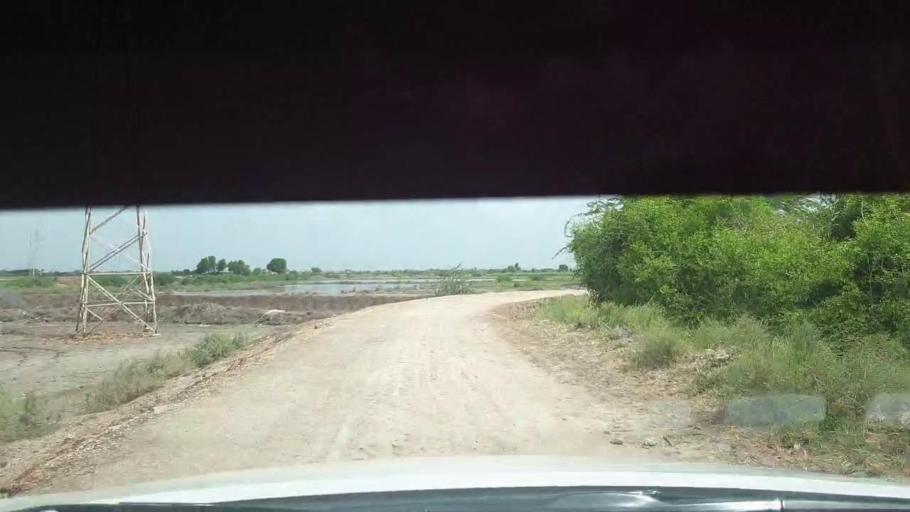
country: PK
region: Sindh
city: Kadhan
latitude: 24.4923
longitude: 68.9818
